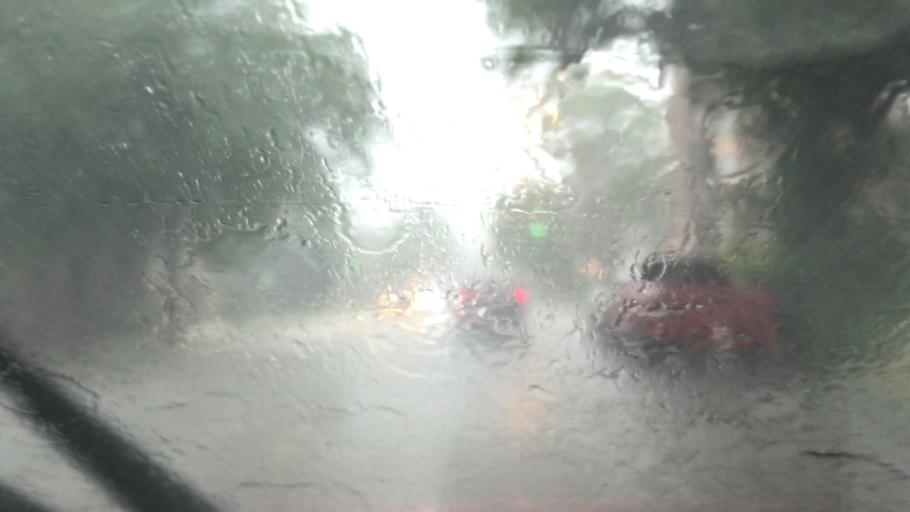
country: US
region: Illinois
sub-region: Cook County
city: Harwood Heights
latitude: 41.9565
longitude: -87.7572
